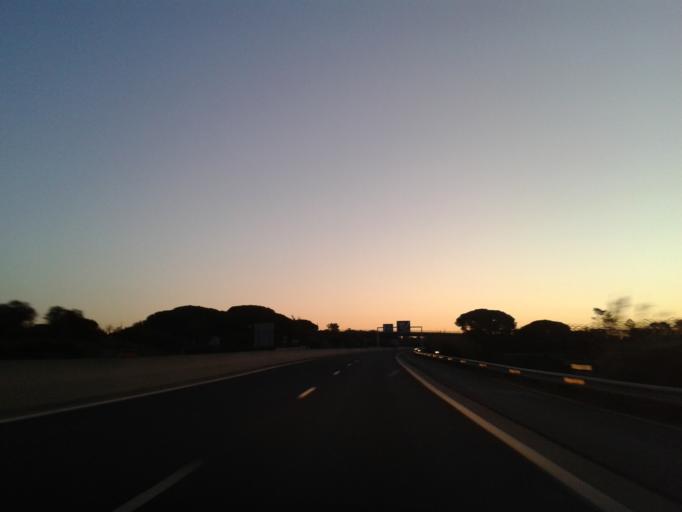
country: PT
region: Faro
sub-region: Albufeira
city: Guia
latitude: 37.1388
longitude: -8.3365
